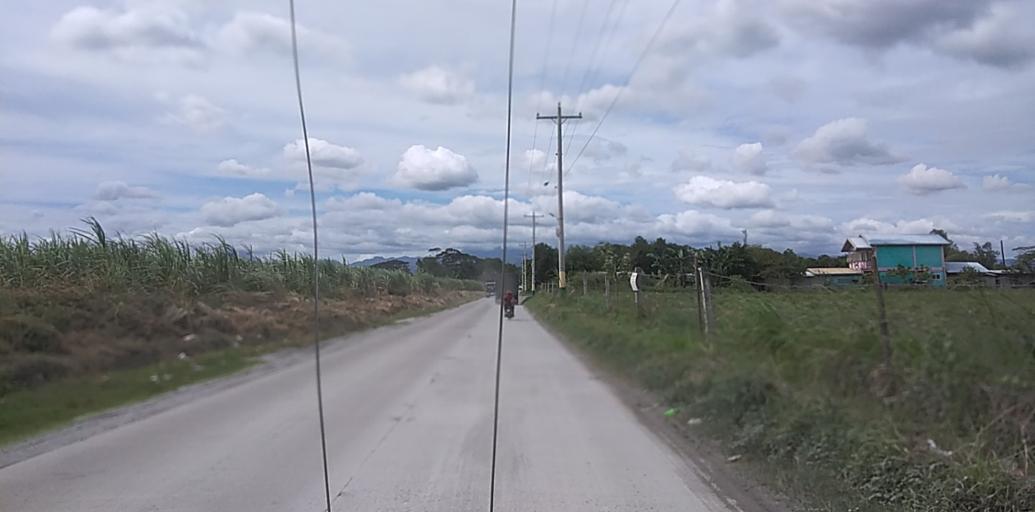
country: PH
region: Central Luzon
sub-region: Province of Pampanga
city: Pulung Santol
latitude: 15.0667
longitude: 120.5672
